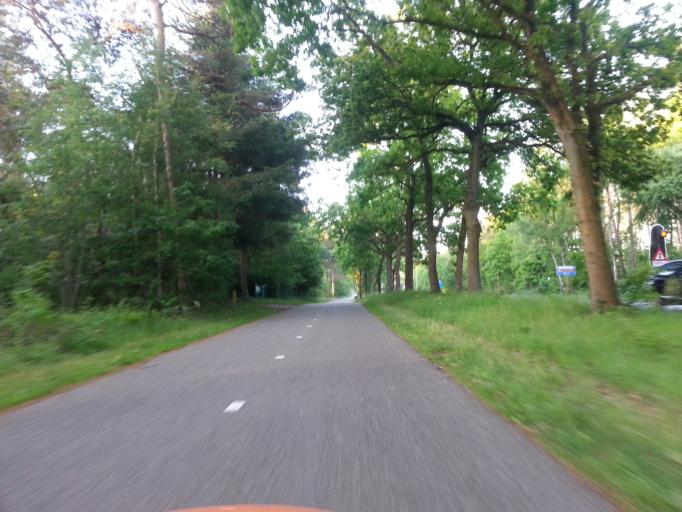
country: NL
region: Utrecht
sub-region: Gemeente Amersfoort
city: Amersfoort
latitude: 52.1237
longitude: 5.3641
